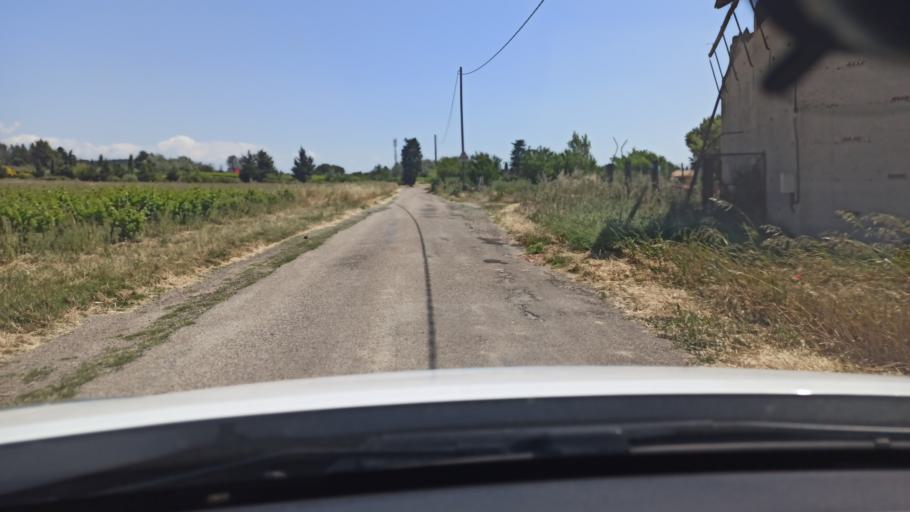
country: FR
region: Provence-Alpes-Cote d'Azur
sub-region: Departement des Bouches-du-Rhone
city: Noves
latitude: 43.9051
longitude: 4.9094
